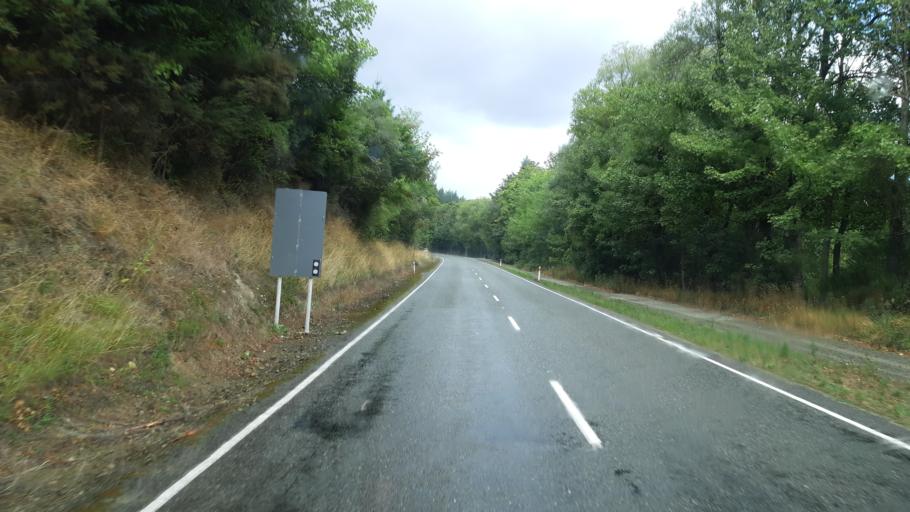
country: NZ
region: Tasman
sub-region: Tasman District
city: Wakefield
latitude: -41.4683
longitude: 172.8410
